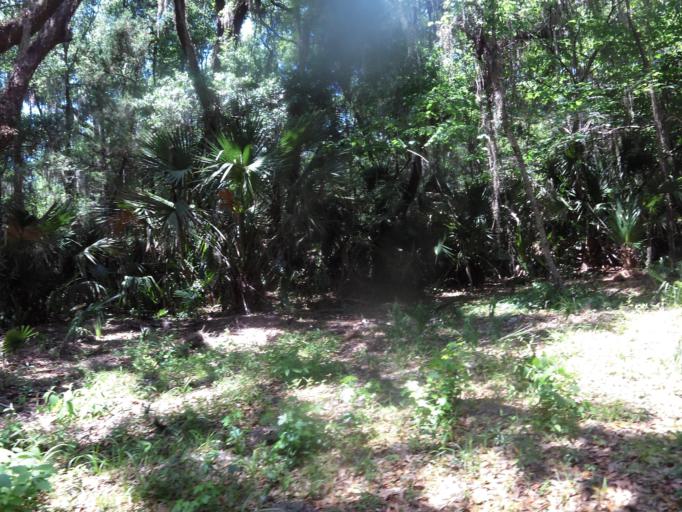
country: US
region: Florida
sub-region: Duval County
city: Atlantic Beach
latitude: 30.4436
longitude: -81.4657
